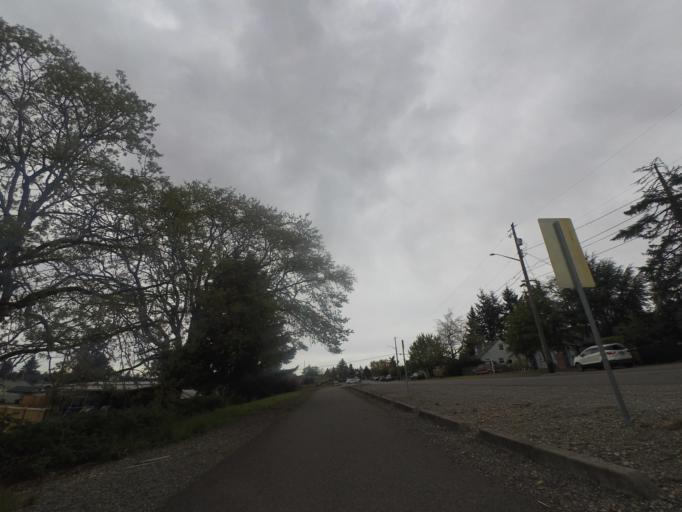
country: US
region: Washington
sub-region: Pierce County
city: Lakewood
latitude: 47.1930
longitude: -122.4756
